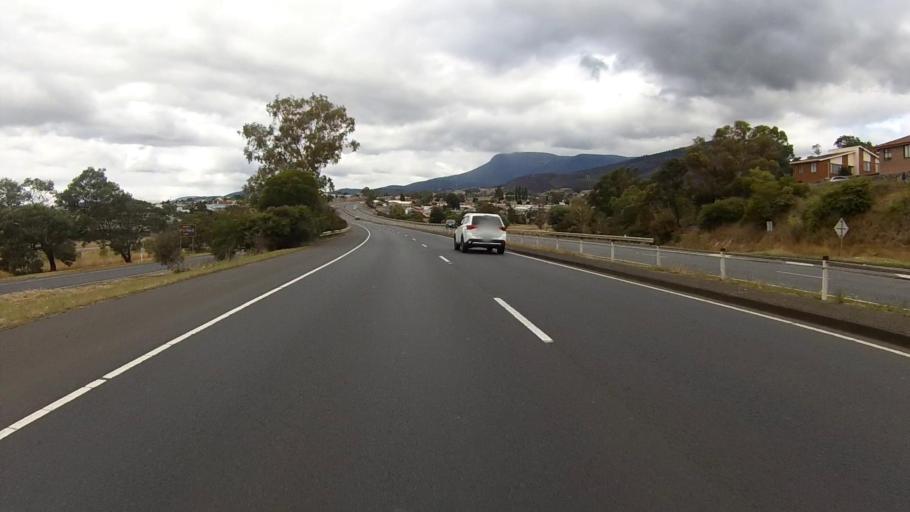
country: AU
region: Tasmania
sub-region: Glenorchy
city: Claremont
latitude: -42.7979
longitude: 147.2485
